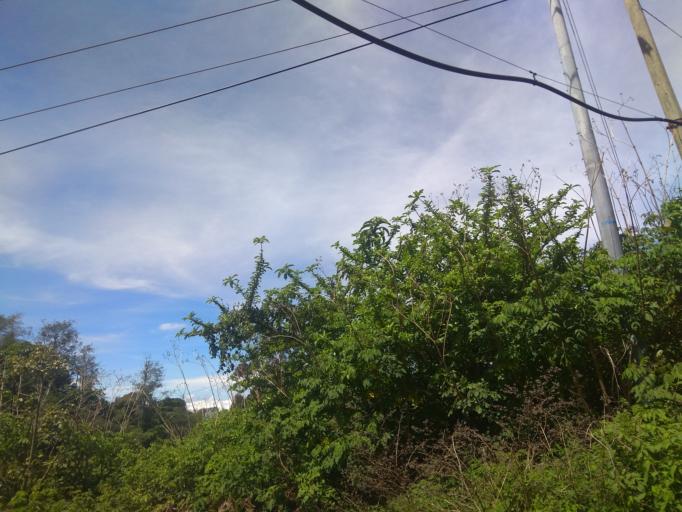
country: CR
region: Cartago
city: Cot
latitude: 9.9238
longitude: -83.9010
